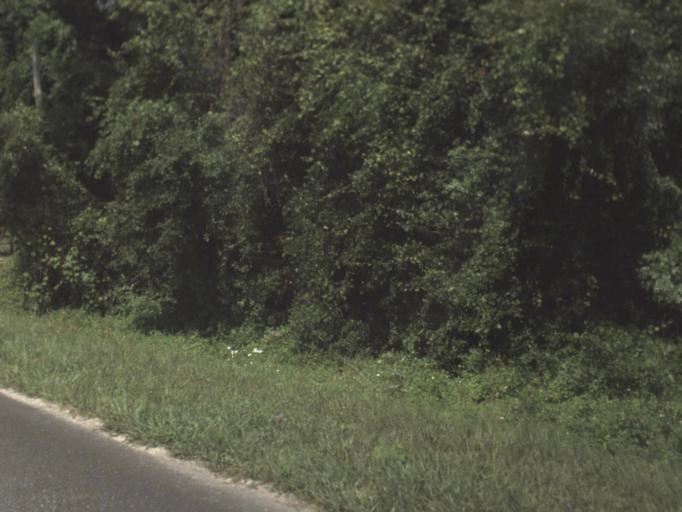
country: US
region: Florida
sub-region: Levy County
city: East Bronson
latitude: 29.4928
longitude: -82.5882
